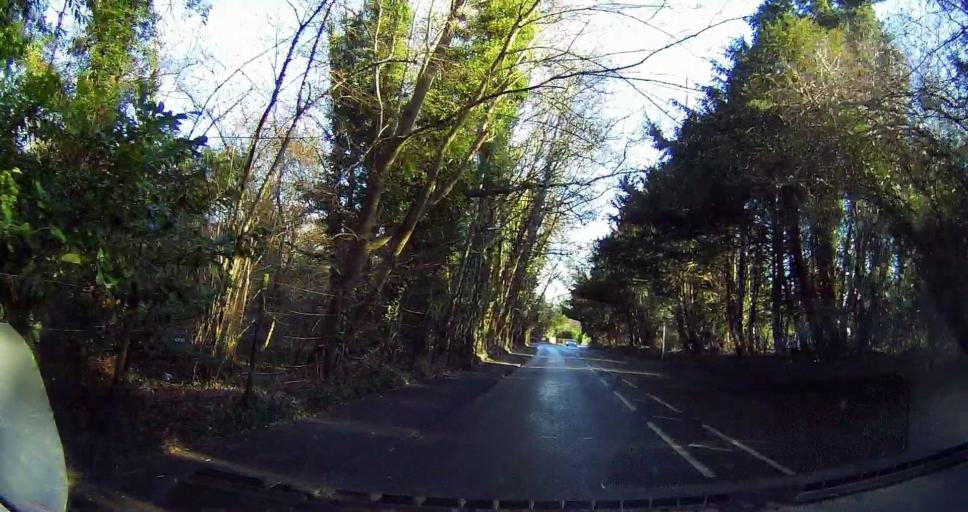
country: GB
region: England
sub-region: Kent
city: Westerham
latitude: 51.2770
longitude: 0.1149
